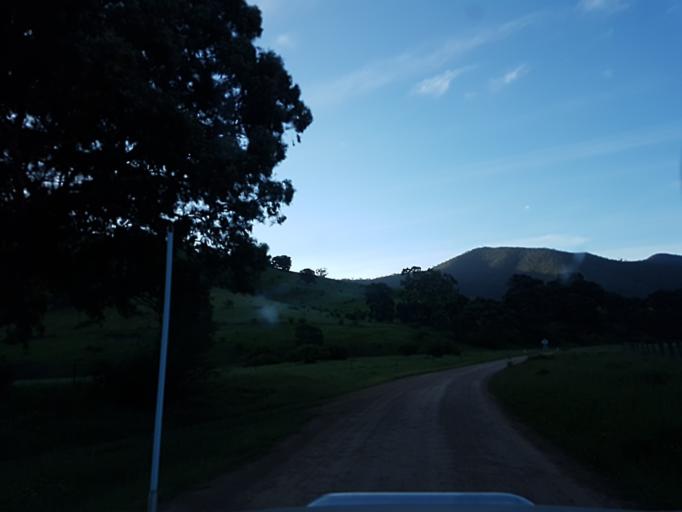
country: AU
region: Victoria
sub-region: East Gippsland
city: Bairnsdale
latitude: -37.4075
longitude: 147.1052
